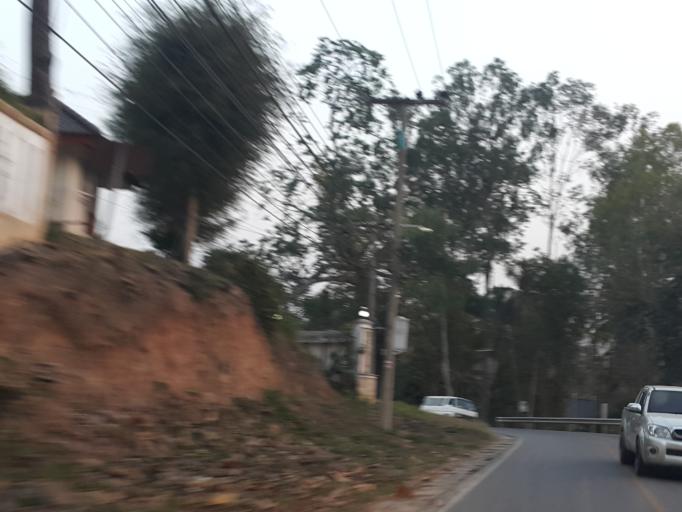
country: TH
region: Chiang Mai
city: Mae Taeng
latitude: 18.9916
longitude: 98.8952
